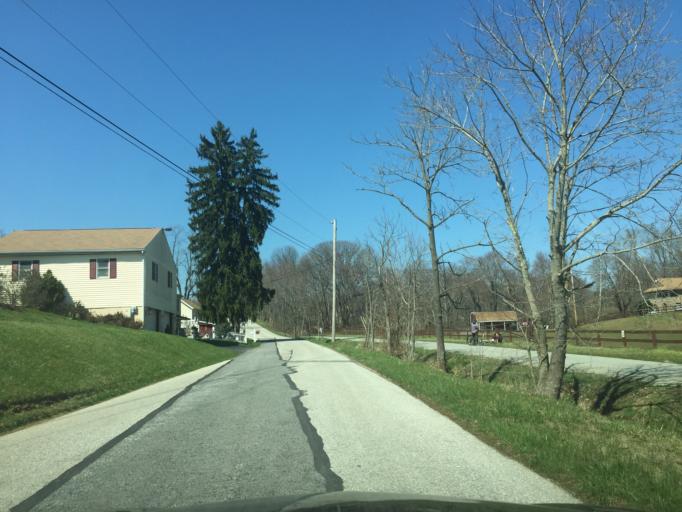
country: US
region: Pennsylvania
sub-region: York County
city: New Freedom
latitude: 39.7225
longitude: -76.6984
